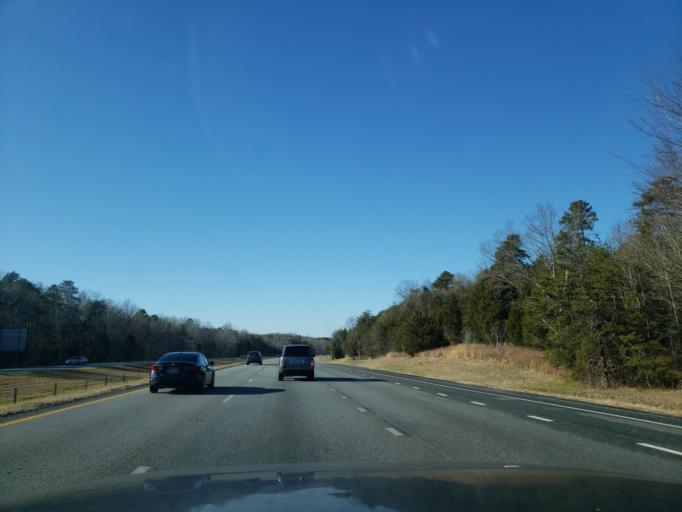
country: US
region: North Carolina
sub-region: Guilford County
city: High Point
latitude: 36.0179
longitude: -80.0445
